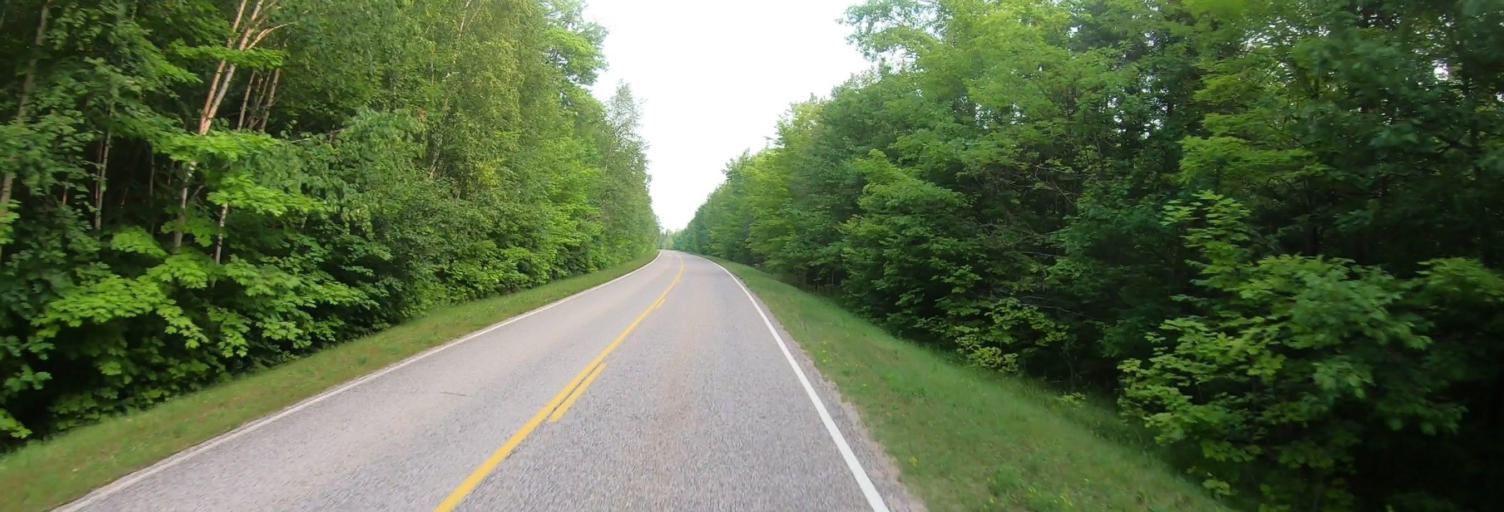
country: US
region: Michigan
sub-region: Chippewa County
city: Sault Ste. Marie
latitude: 46.4598
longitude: -84.8564
